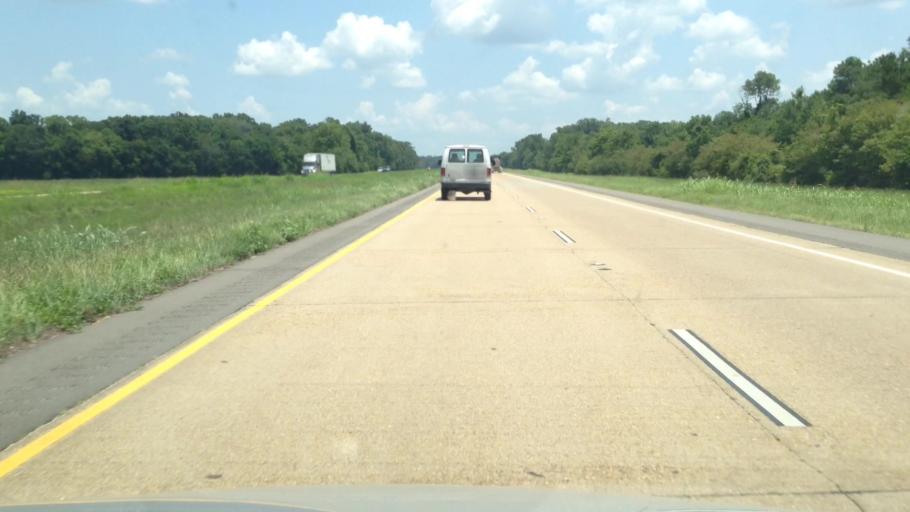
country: US
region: Louisiana
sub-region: Rapides Parish
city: Lecompte
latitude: 31.0086
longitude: -92.3612
